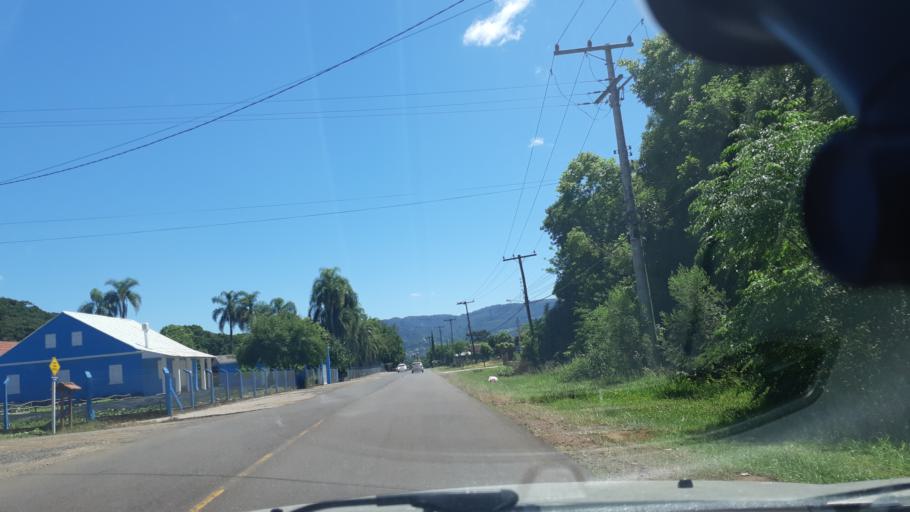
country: BR
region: Rio Grande do Sul
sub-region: Ivoti
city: Ivoti
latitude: -29.6130
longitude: -51.0919
